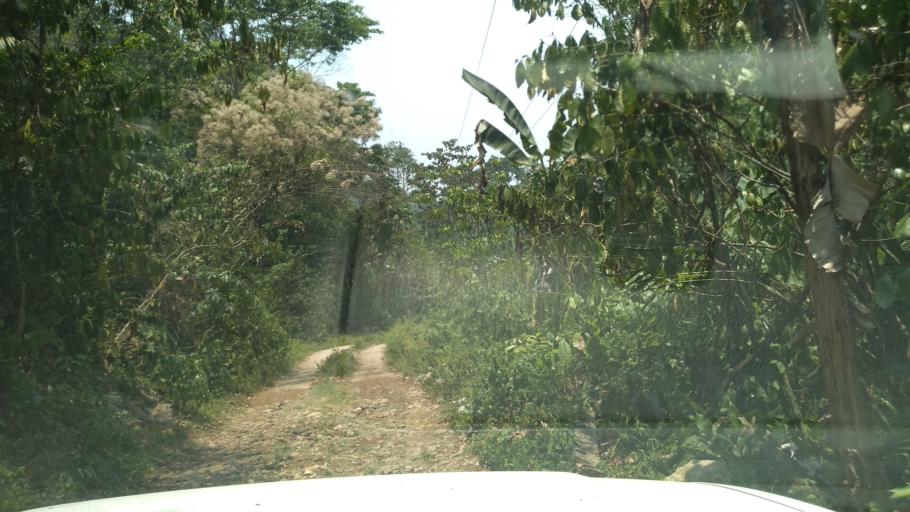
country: MX
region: Veracruz
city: Motzorongo
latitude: 18.5991
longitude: -96.7404
